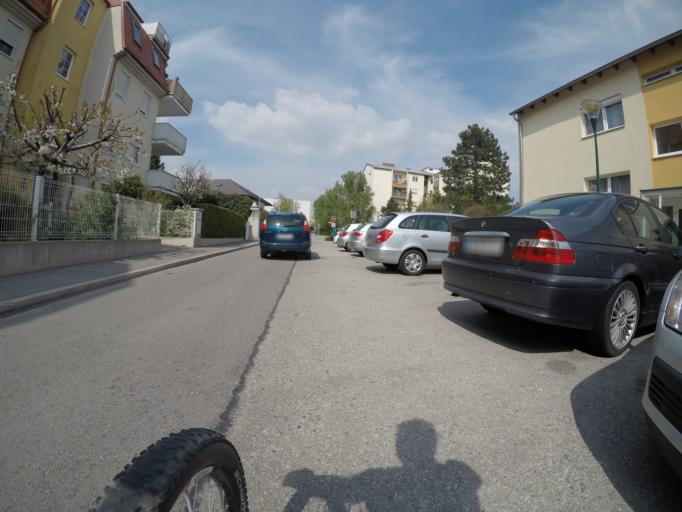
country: AT
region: Lower Austria
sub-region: Politischer Bezirk Modling
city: Wiener Neudorf
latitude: 48.0861
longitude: 16.3093
